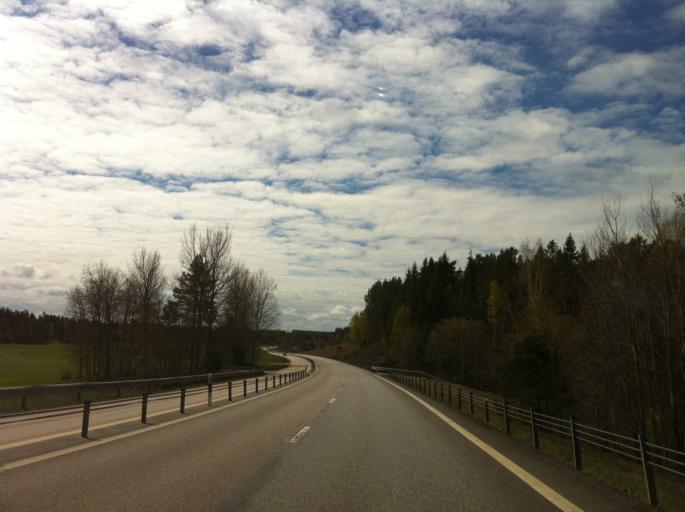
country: SE
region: OEstergoetland
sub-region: Valdemarsviks Kommun
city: Valdemarsvik
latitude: 58.1936
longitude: 16.5964
